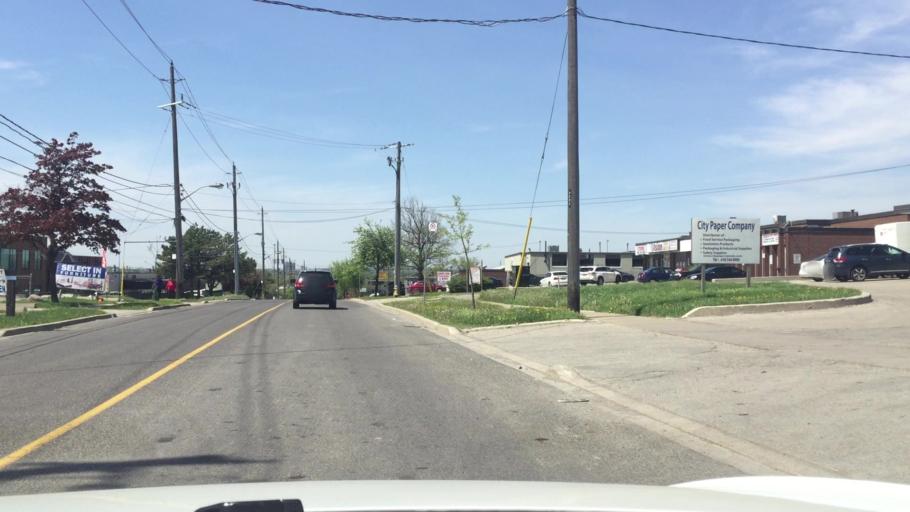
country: CA
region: Ontario
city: Concord
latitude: 43.7477
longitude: -79.5224
